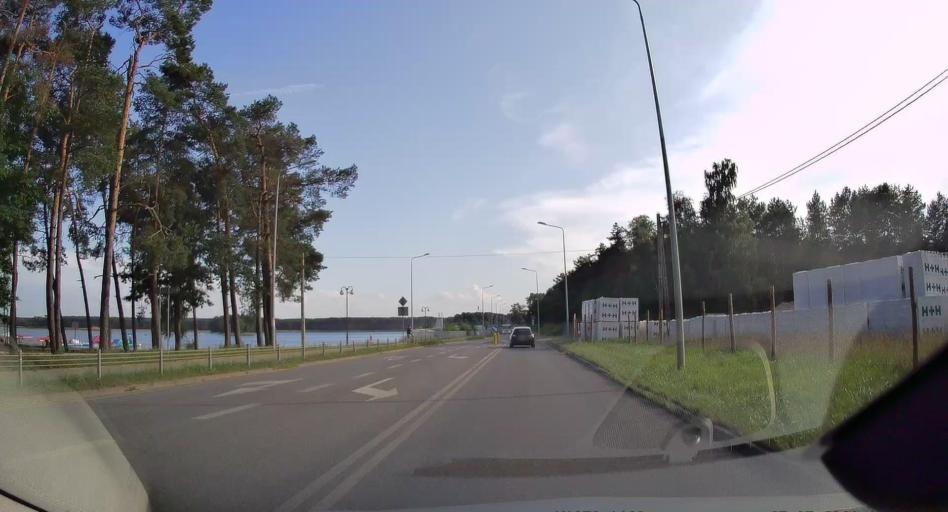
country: PL
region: Swietokrzyskie
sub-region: Powiat konecki
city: Smykow
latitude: 51.1184
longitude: 20.3519
